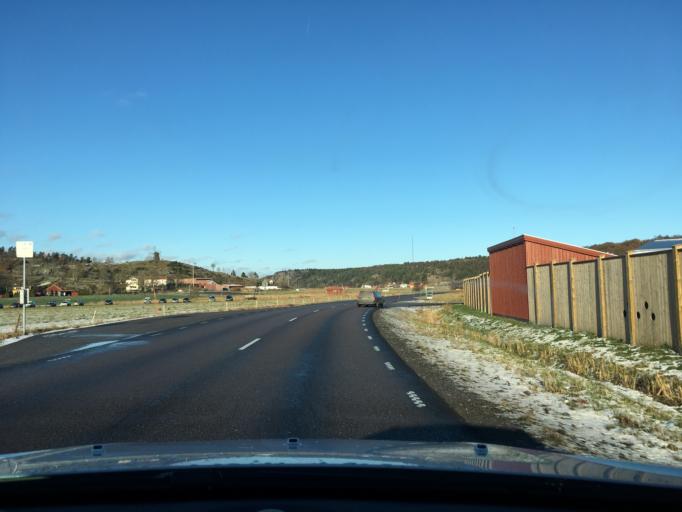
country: SE
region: Vaestra Goetaland
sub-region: Tjorns Kommun
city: Myggenas
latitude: 58.0284
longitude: 11.6563
